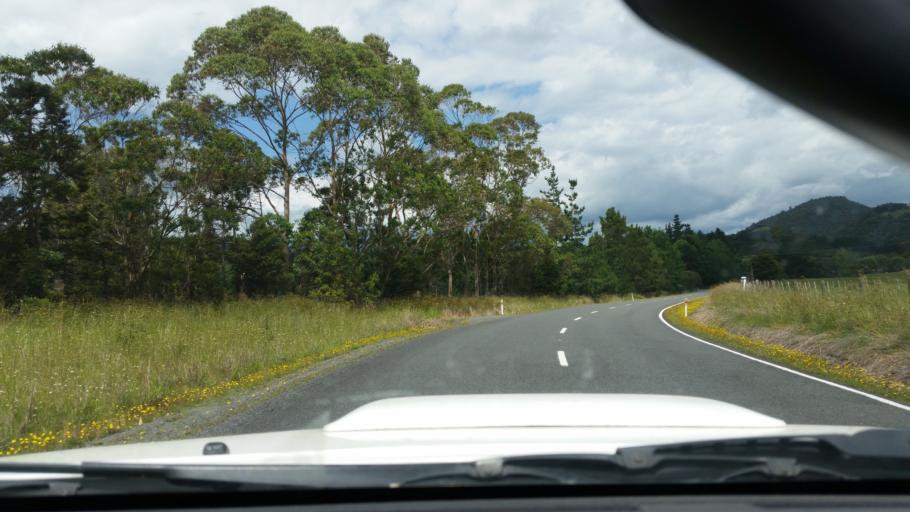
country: NZ
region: Northland
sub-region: Kaipara District
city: Dargaville
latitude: -35.7498
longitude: 173.8985
